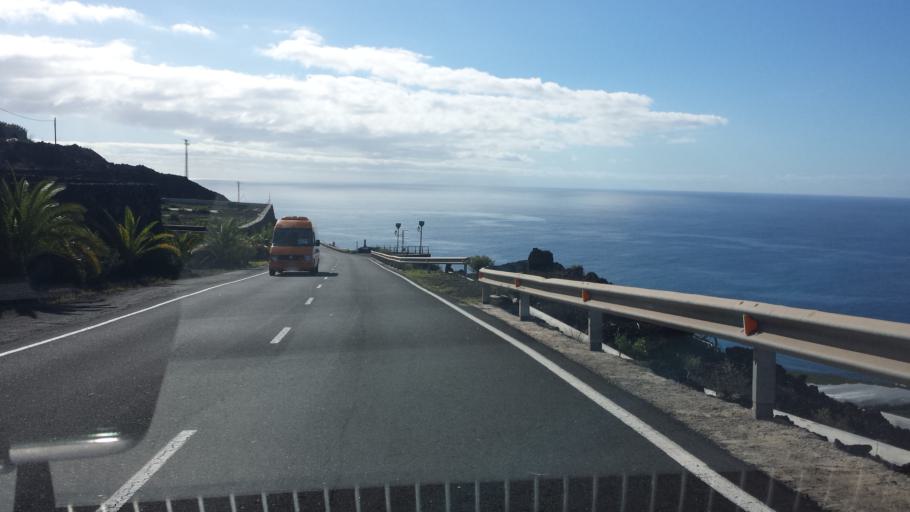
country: ES
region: Canary Islands
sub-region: Provincia de Santa Cruz de Tenerife
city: Tazacorte
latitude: 28.5973
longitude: -17.9122
